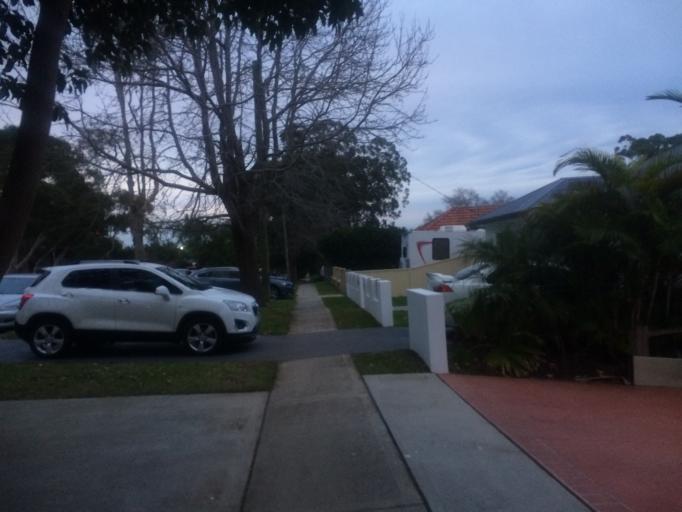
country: AU
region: New South Wales
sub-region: Sutherland Shire
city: Kirrawee
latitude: -34.0302
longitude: 151.0674
